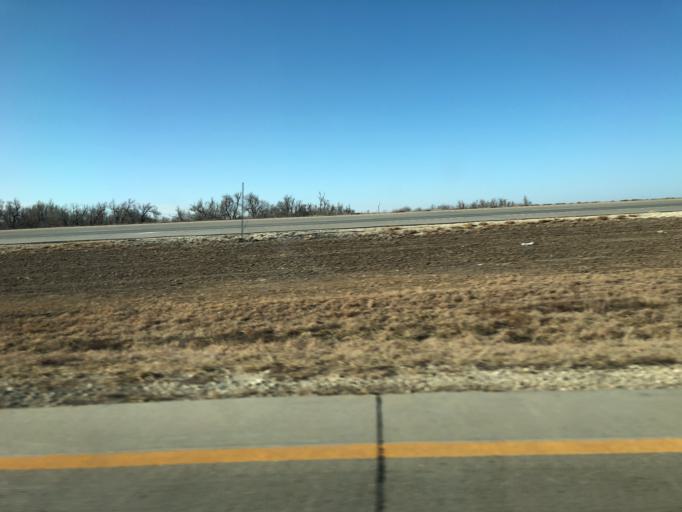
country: US
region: Kansas
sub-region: Reno County
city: South Hutchinson
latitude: 38.0256
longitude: -97.9067
